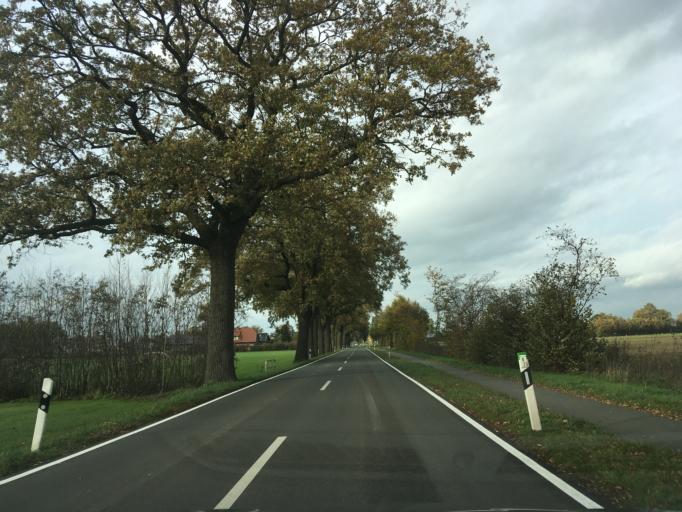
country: DE
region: North Rhine-Westphalia
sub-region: Regierungsbezirk Munster
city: Vreden
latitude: 52.0957
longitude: 6.8864
